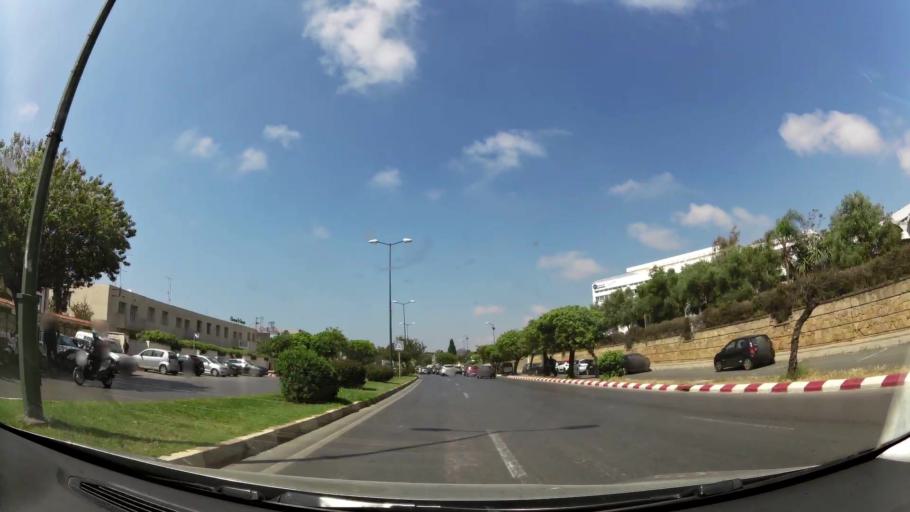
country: MA
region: Rabat-Sale-Zemmour-Zaer
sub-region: Rabat
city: Rabat
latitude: 33.9912
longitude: -6.8465
